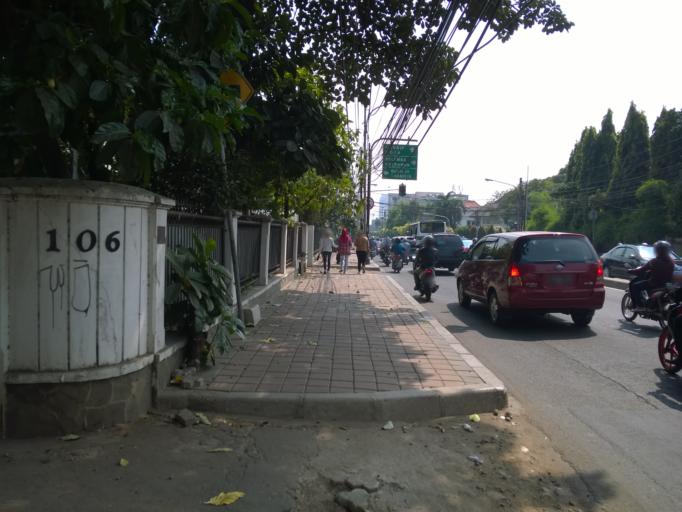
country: ID
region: Jakarta Raya
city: Jakarta
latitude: -6.2003
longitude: 106.8281
